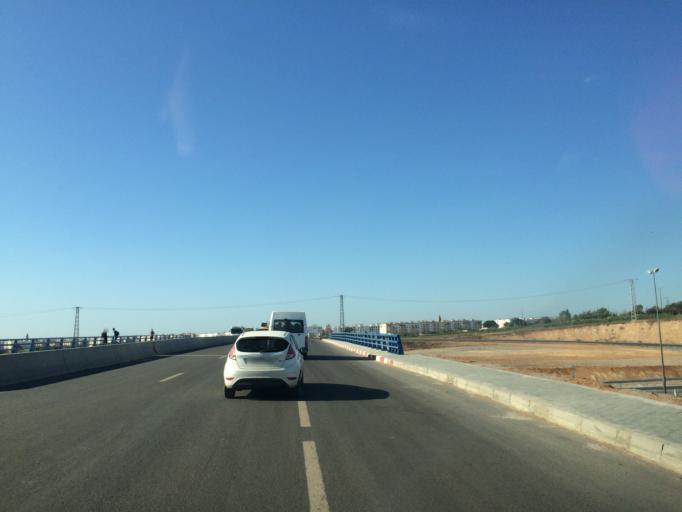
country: MA
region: Rabat-Sale-Zemmour-Zaer
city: Sale
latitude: 33.9804
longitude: -6.7404
